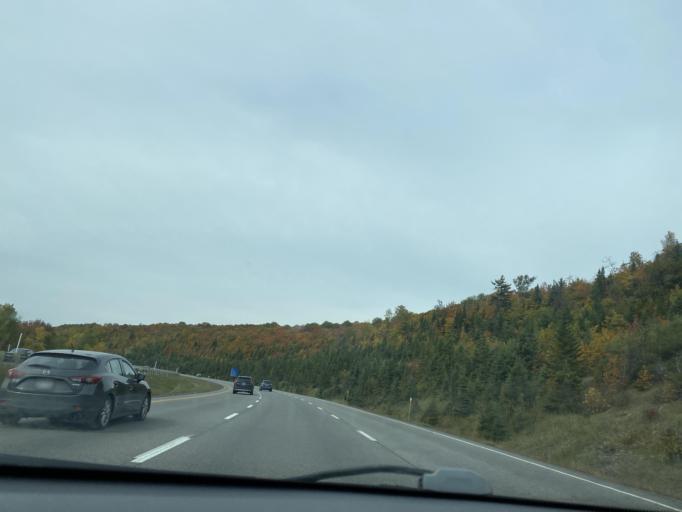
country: CA
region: Quebec
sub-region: Laurentides
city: Sainte-Adele
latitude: 45.9799
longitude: -74.1637
